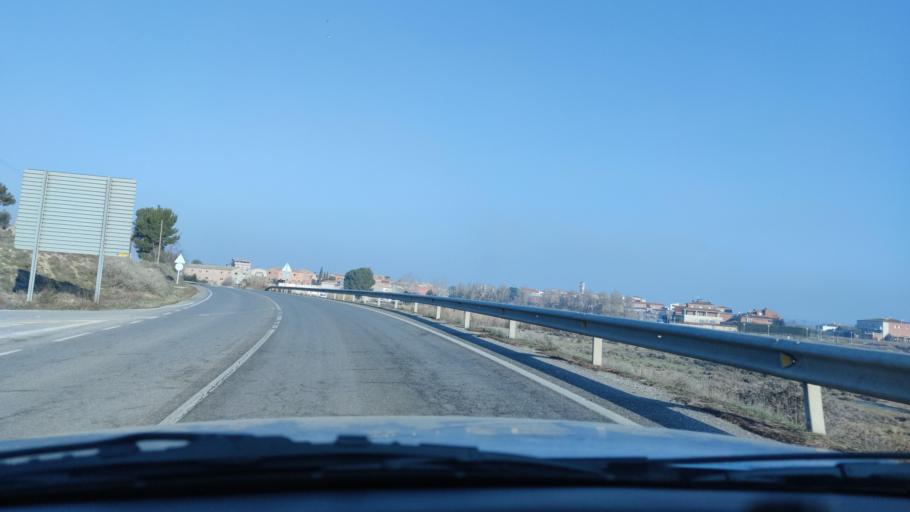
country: ES
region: Catalonia
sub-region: Provincia de Lleida
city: Torrefarrera
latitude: 41.6668
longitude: 0.6293
